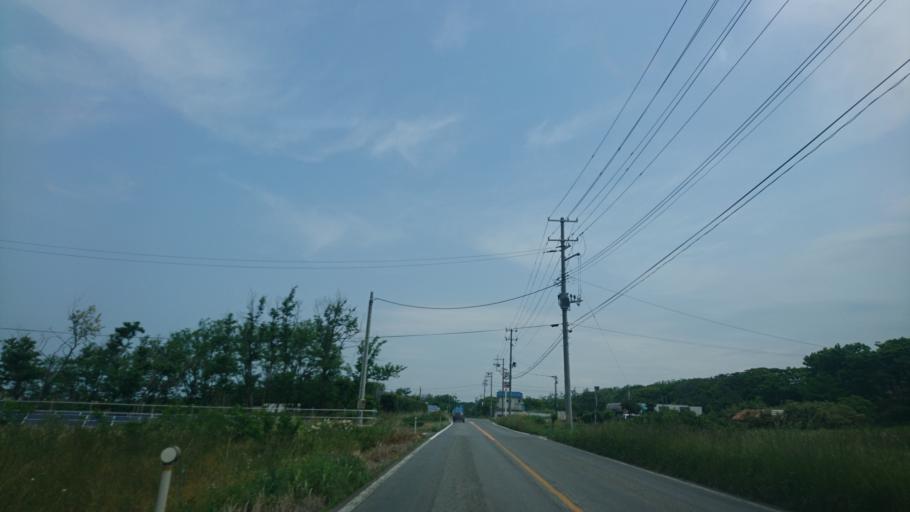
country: JP
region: Niigata
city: Shibata
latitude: 38.0371
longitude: 139.3014
